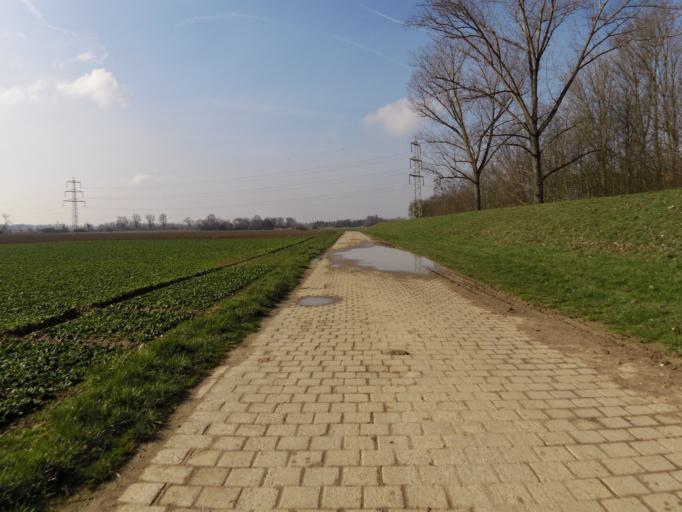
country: DE
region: Rheinland-Pfalz
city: Bobenheim-Roxheim
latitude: 49.5915
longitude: 8.3991
